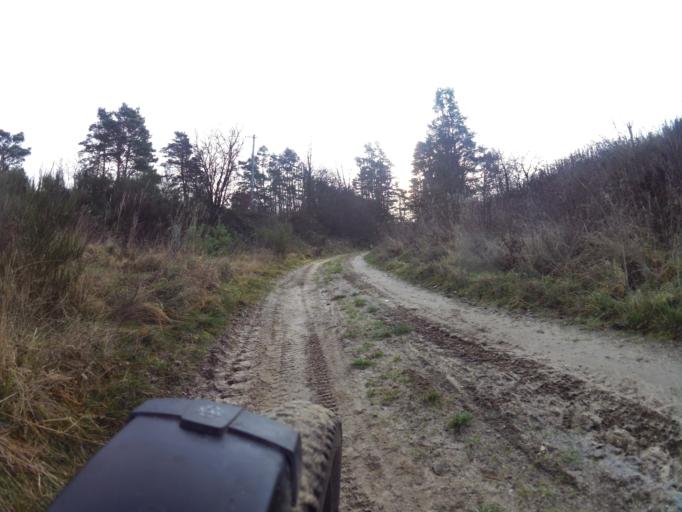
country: PL
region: West Pomeranian Voivodeship
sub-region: Powiat koszalinski
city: Polanow
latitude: 54.1955
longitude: 16.7244
